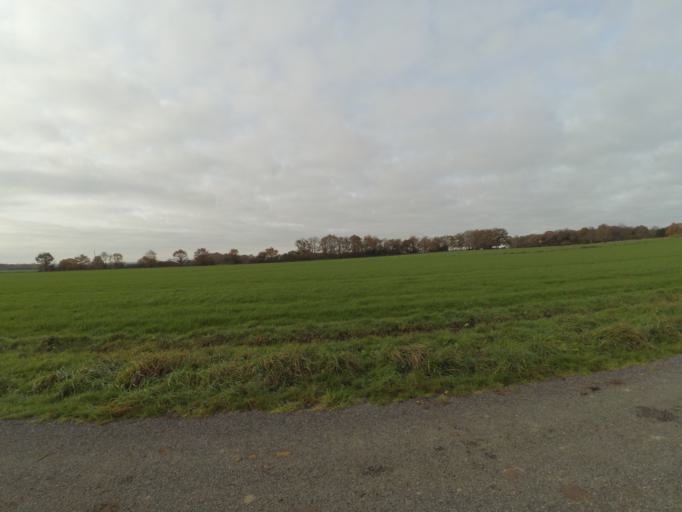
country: FR
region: Pays de la Loire
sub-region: Departement de la Loire-Atlantique
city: La Planche
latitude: 47.0101
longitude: -1.3921
